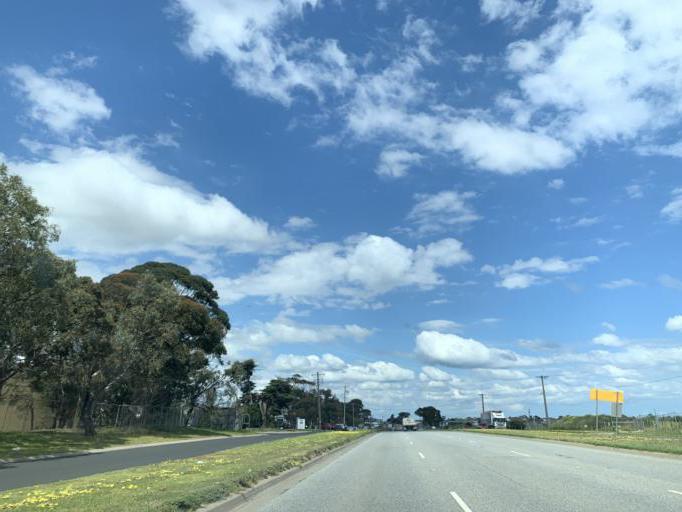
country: AU
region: Victoria
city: Heatherton
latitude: -37.9813
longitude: 145.1104
